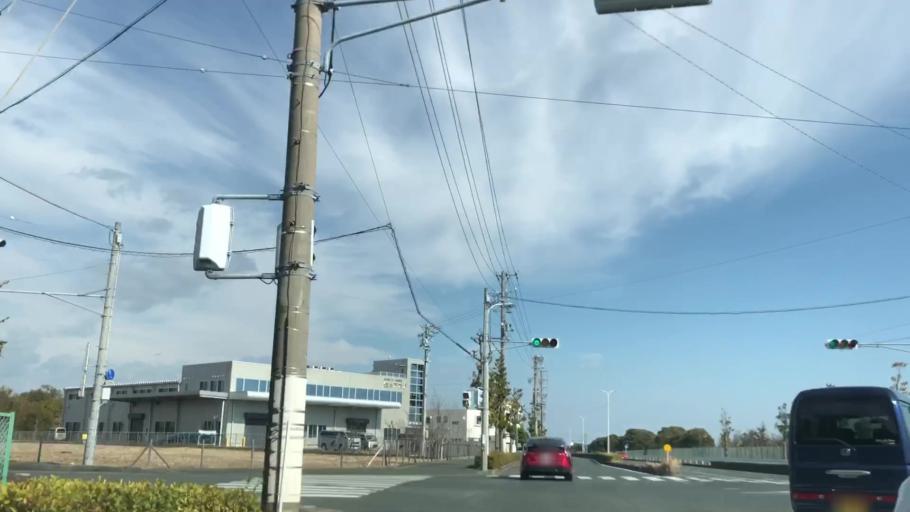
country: JP
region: Shizuoka
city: Hamamatsu
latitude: 34.7534
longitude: 137.7023
